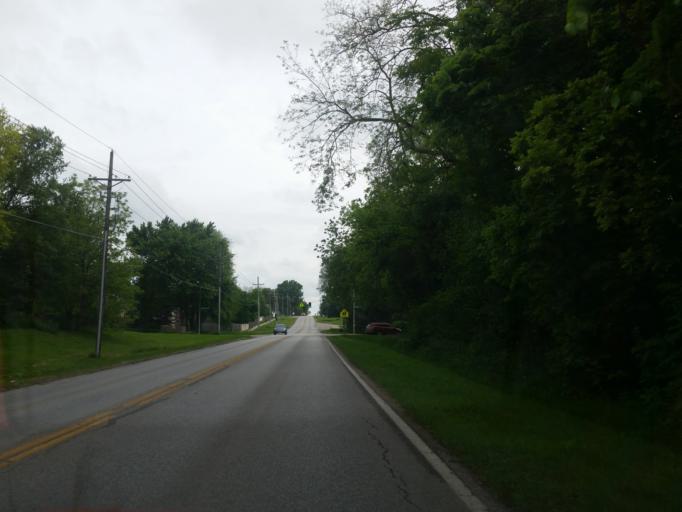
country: US
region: Nebraska
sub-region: Sarpy County
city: Offutt Air Force Base
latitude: 41.1123
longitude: -95.9666
